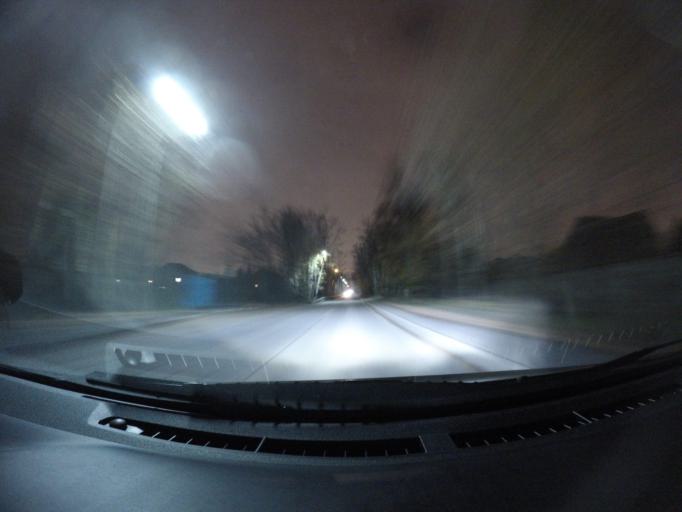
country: RU
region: Moscow
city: Zyablikovo
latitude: 55.5919
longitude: 37.7851
